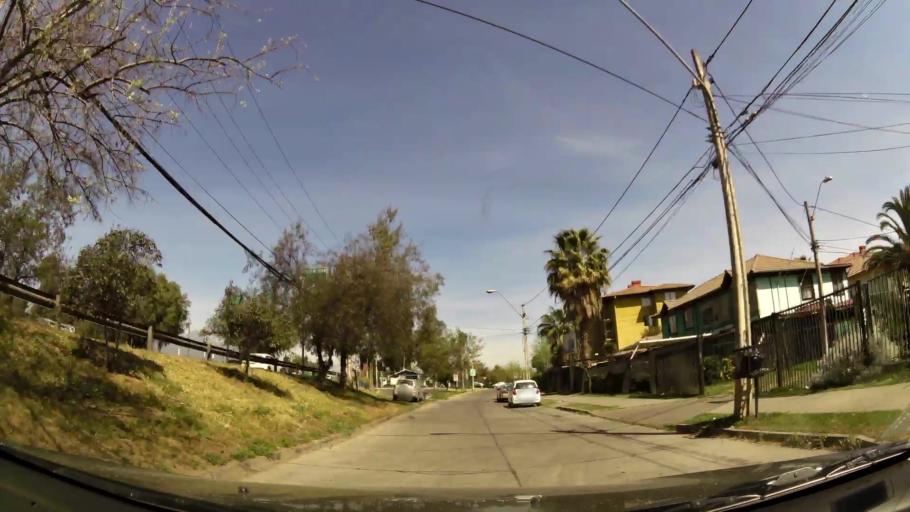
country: CL
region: Santiago Metropolitan
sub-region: Provincia de Cordillera
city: Puente Alto
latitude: -33.5653
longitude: -70.5554
